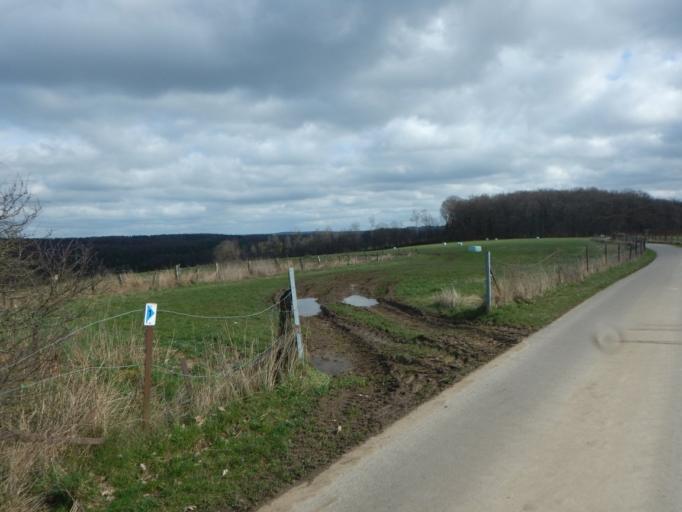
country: LU
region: Luxembourg
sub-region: Canton de Mersch
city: Tuntange
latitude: 49.7209
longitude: 6.0379
